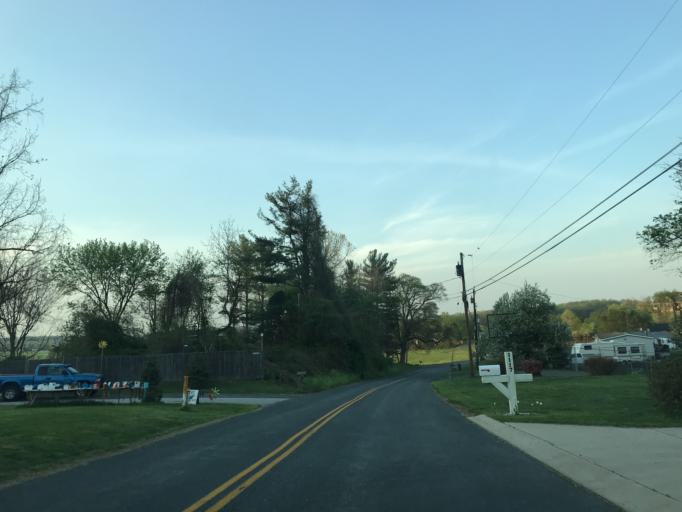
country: US
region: Maryland
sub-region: Harford County
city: Jarrettsville
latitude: 39.6043
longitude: -76.4144
